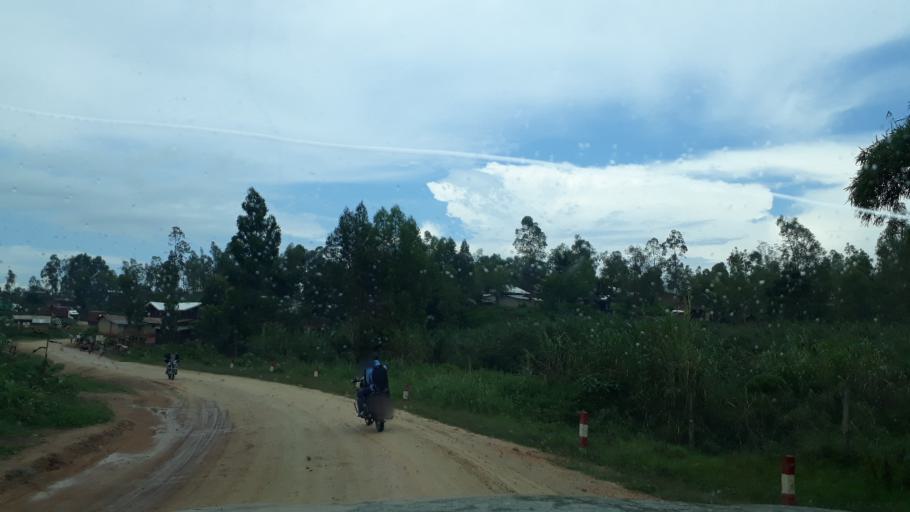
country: CD
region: Eastern Province
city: Bunia
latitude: 1.6365
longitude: 30.2663
